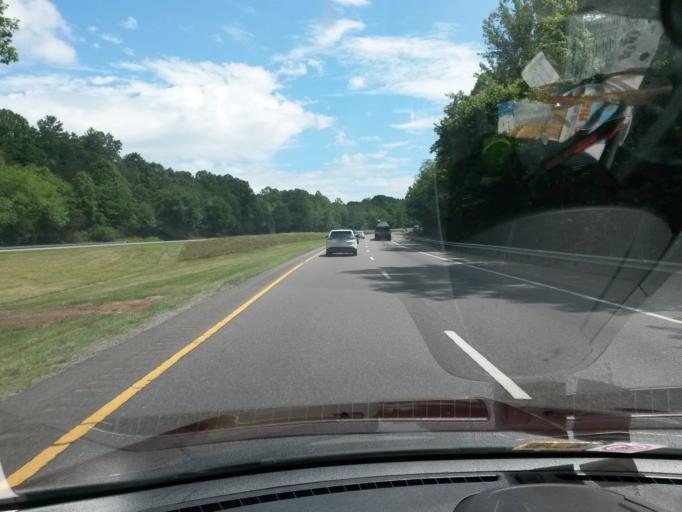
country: US
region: North Carolina
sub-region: Surry County
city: Dobson
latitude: 36.4298
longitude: -80.7766
